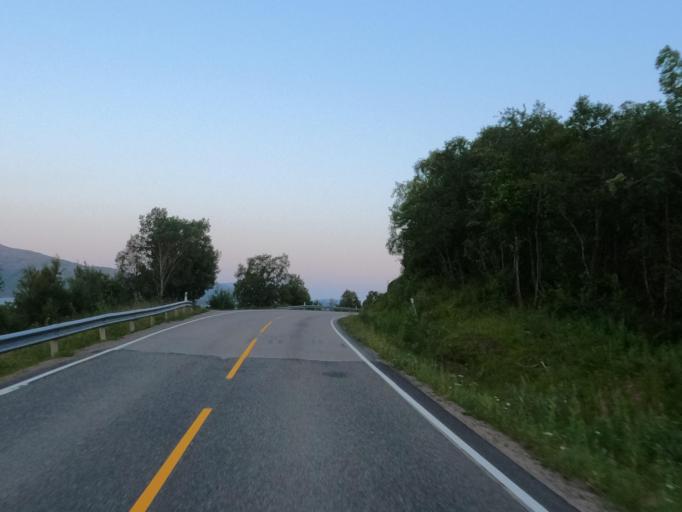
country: NO
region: Nordland
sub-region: Lodingen
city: Lodingen
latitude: 68.5063
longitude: 16.0966
